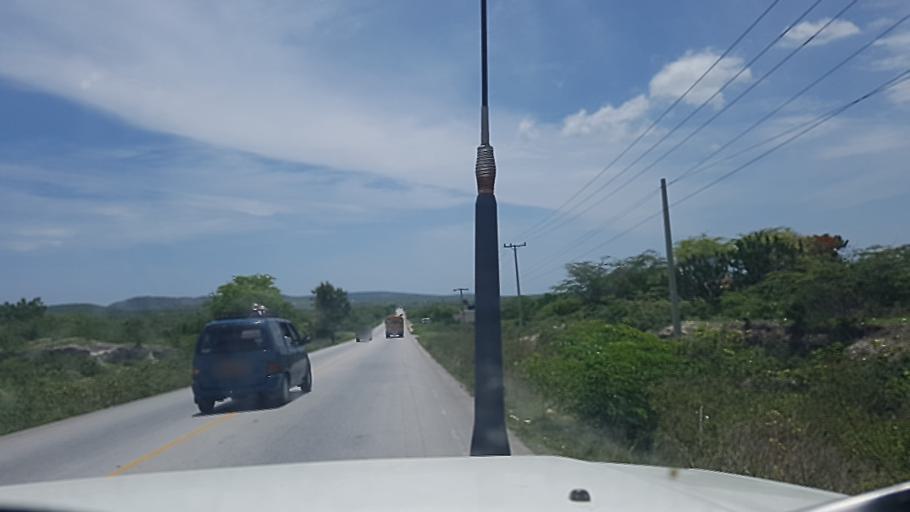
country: HT
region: Artibonite
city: Saint-Marc
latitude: 19.1522
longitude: -72.6358
